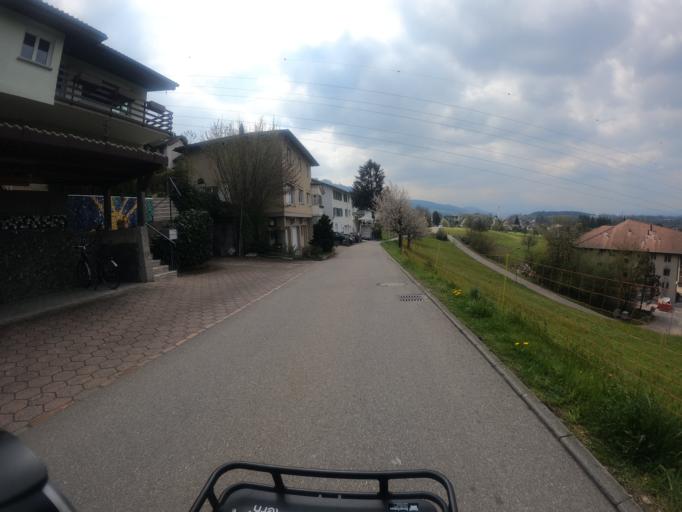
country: CH
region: Lucerne
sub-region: Lucerne-Land District
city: Root
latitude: 47.1222
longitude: 8.3980
